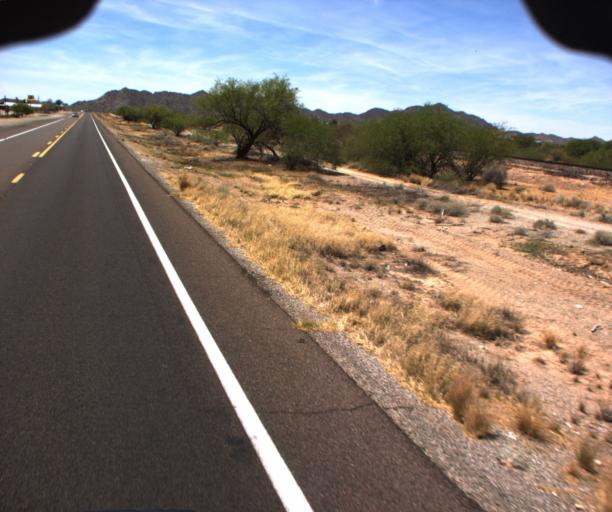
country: US
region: Arizona
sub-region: La Paz County
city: Salome
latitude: 33.7638
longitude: -113.6471
